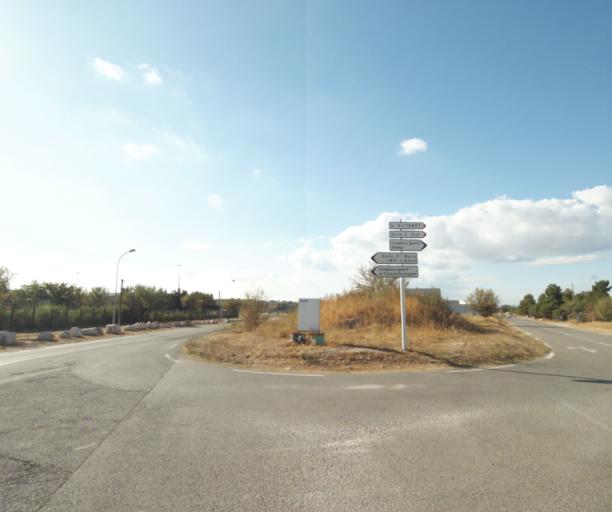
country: FR
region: Provence-Alpes-Cote d'Azur
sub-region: Departement des Bouches-du-Rhone
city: Saint-Victoret
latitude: 43.4116
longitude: 5.2443
